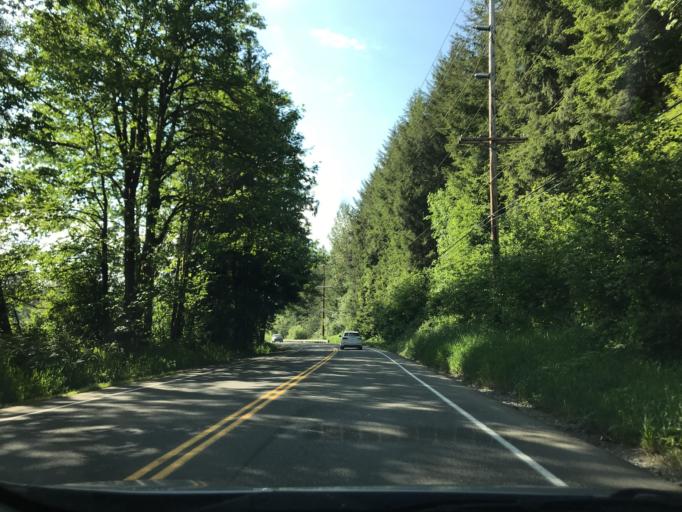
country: US
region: Washington
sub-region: King County
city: Hobart
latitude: 47.4411
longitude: -121.9831
